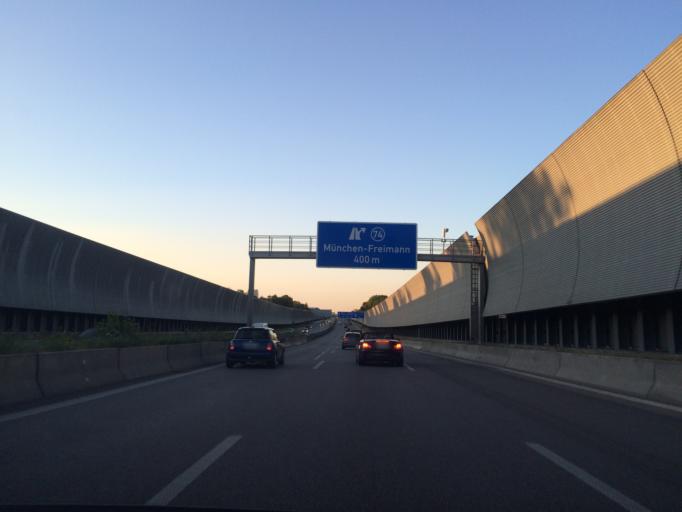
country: DE
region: Bavaria
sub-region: Upper Bavaria
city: Unterfoehring
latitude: 48.1901
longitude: 11.6139
